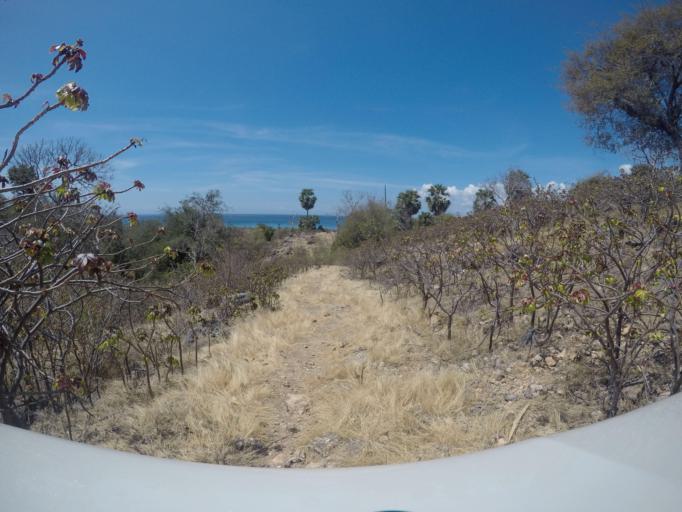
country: TL
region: Baucau
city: Baucau
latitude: -8.4330
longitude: 126.4419
